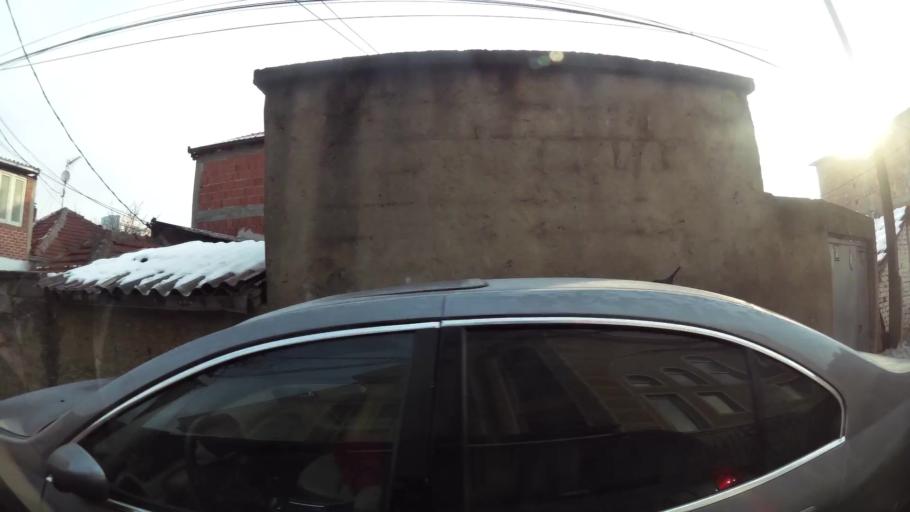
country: MK
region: Cair
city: Cair
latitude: 42.0186
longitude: 21.4385
